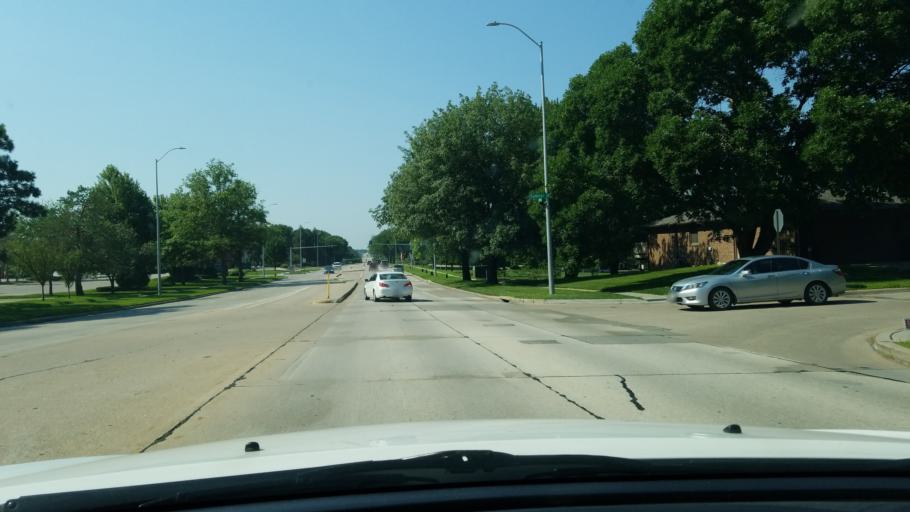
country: US
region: Nebraska
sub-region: Lancaster County
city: Lincoln
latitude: 40.7959
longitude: -96.6251
